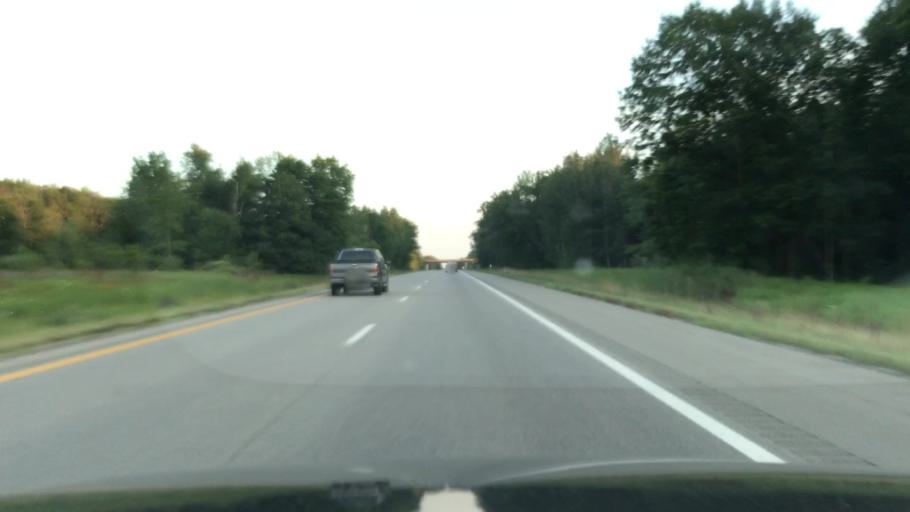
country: US
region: Michigan
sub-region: Montcalm County
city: Howard City
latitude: 43.5317
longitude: -85.4868
